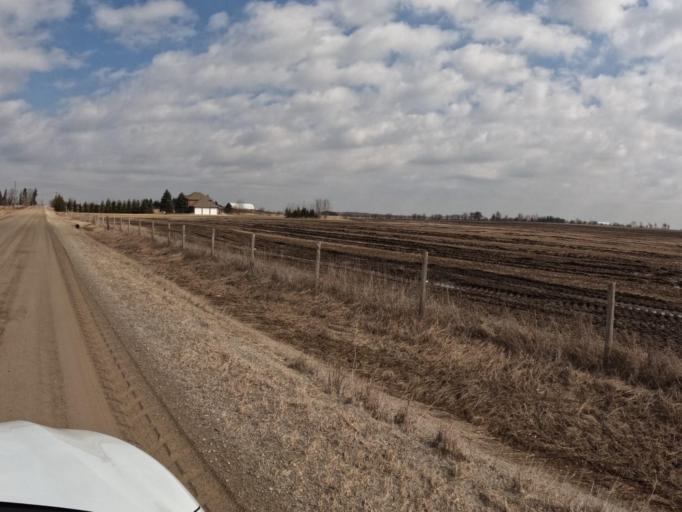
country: CA
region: Ontario
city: Orangeville
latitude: 43.9105
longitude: -80.2374
